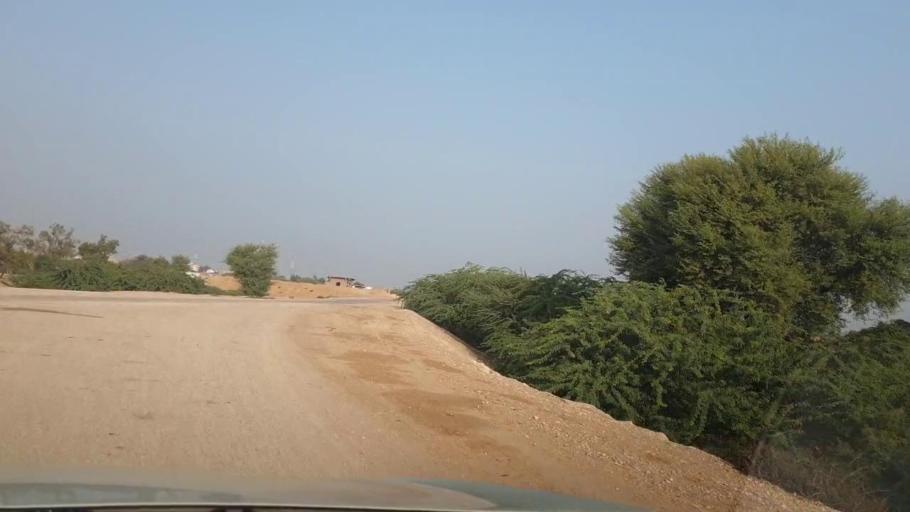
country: PK
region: Sindh
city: Sehwan
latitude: 26.3374
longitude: 67.7280
